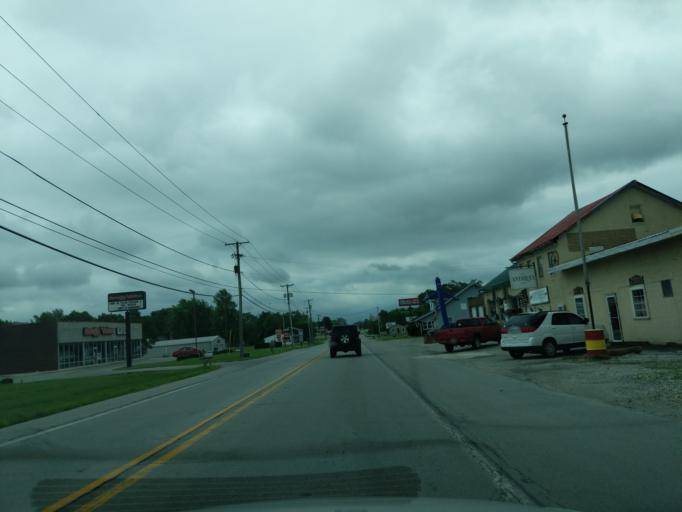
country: US
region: Indiana
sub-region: Madison County
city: Elwood
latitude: 40.2770
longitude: -85.8205
